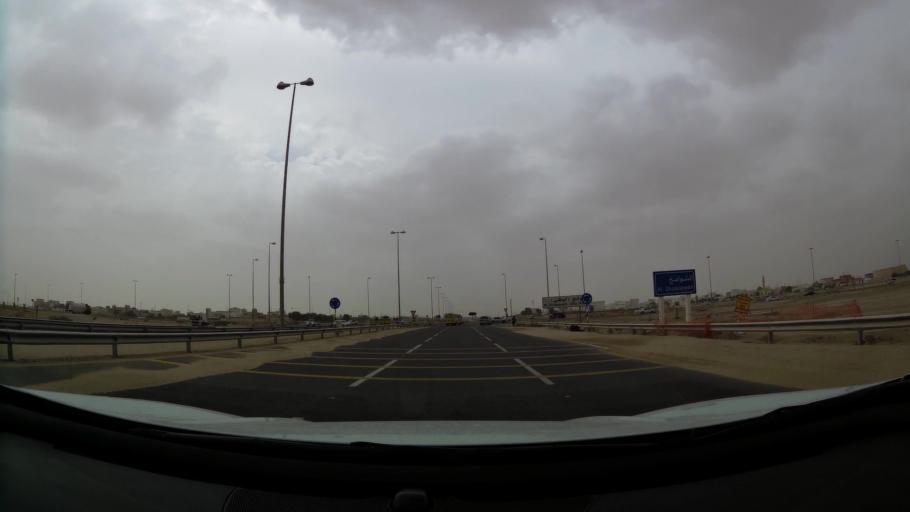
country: AE
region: Abu Dhabi
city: Abu Dhabi
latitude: 24.3662
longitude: 54.6610
